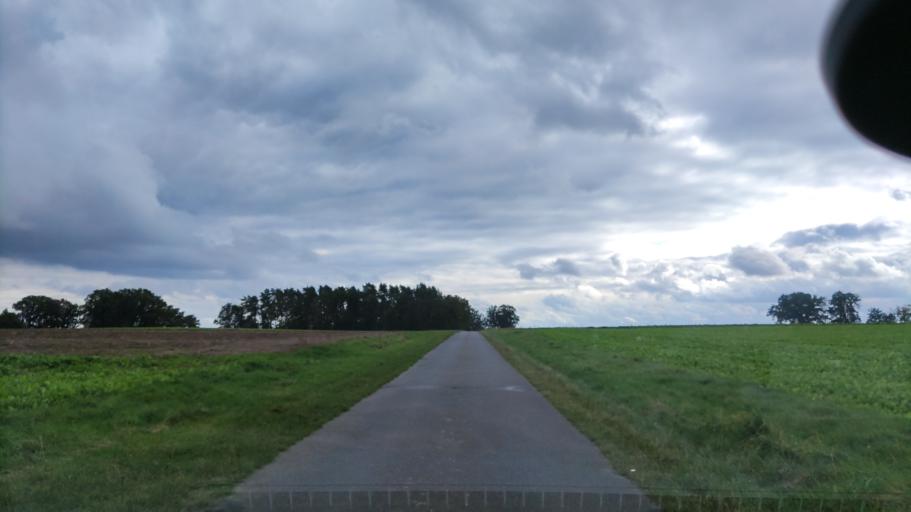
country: DE
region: Lower Saxony
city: Vastorf
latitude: 53.1603
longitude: 10.5338
